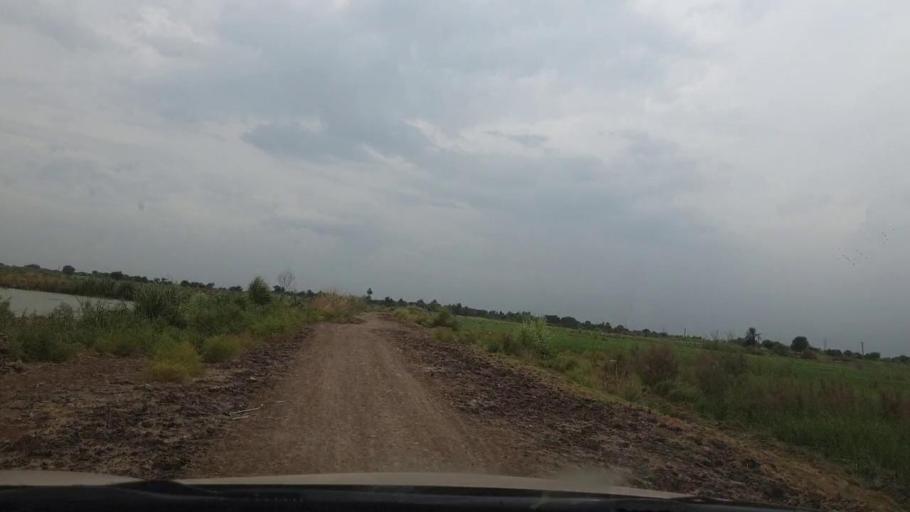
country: PK
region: Sindh
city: Ratodero
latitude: 27.8022
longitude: 68.3136
